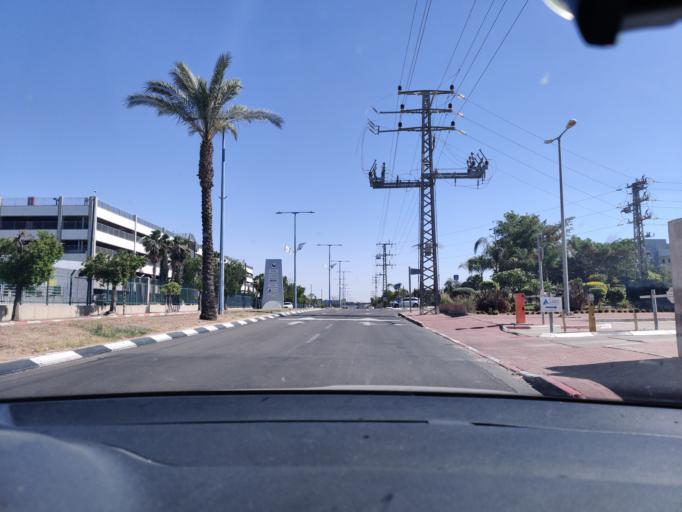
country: IL
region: Southern District
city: Qiryat Gat
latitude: 31.5956
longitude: 34.7862
